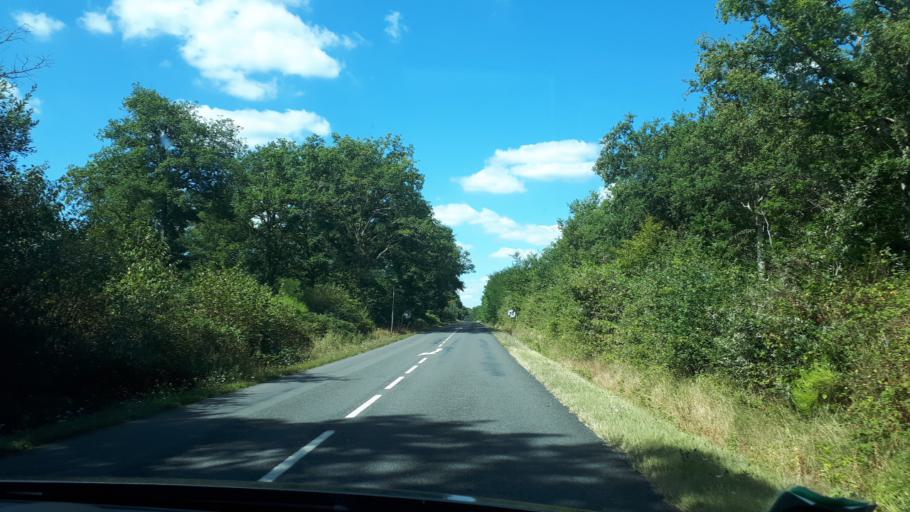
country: FR
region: Centre
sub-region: Departement du Loir-et-Cher
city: Neung-sur-Beuvron
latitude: 47.5344
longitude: 1.7608
